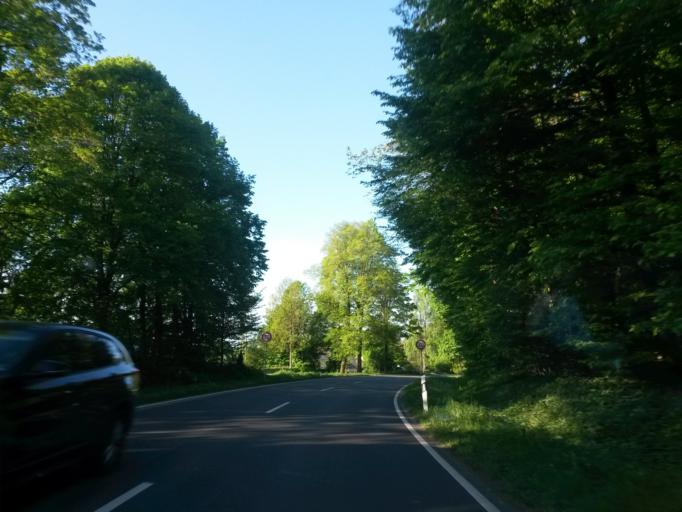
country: DE
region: North Rhine-Westphalia
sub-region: Regierungsbezirk Koln
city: Numbrecht
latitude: 50.9231
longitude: 7.4973
